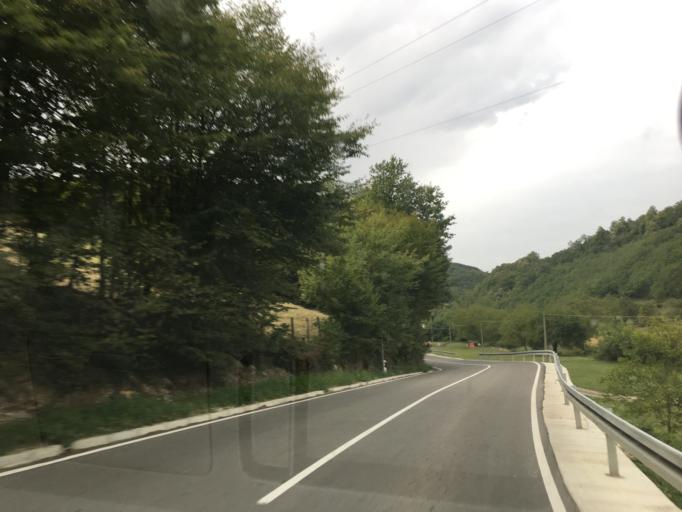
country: RS
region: Central Serbia
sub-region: Sumadijski Okrug
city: Arangelovac
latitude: 44.1713
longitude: 20.5203
